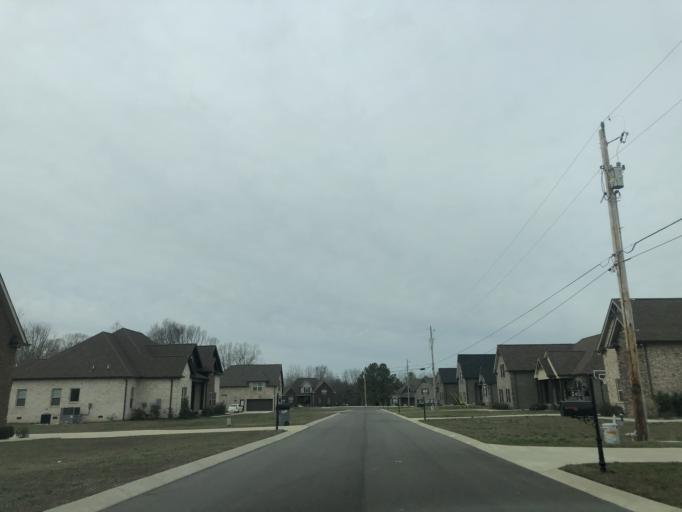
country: US
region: Tennessee
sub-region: Robertson County
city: Greenbrier
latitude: 36.4033
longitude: -86.8206
